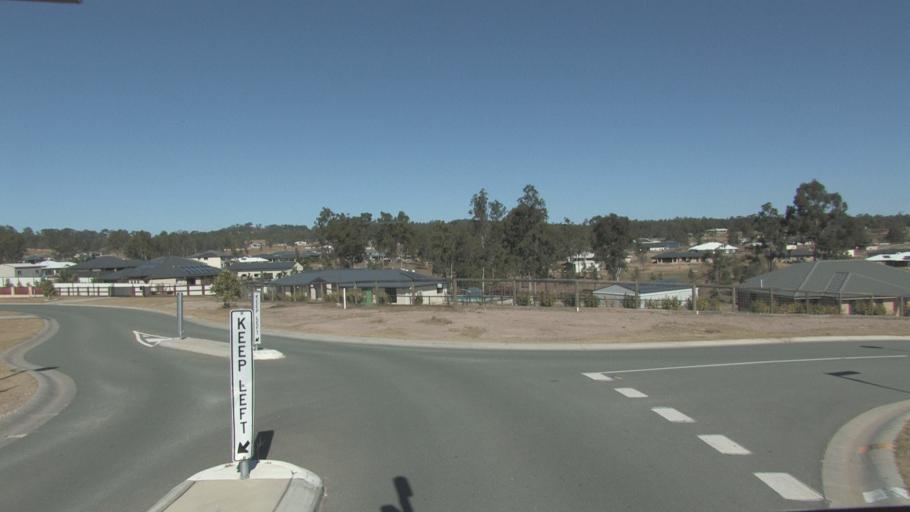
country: AU
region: Queensland
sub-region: Logan
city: Cedar Vale
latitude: -27.8674
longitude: 153.0474
